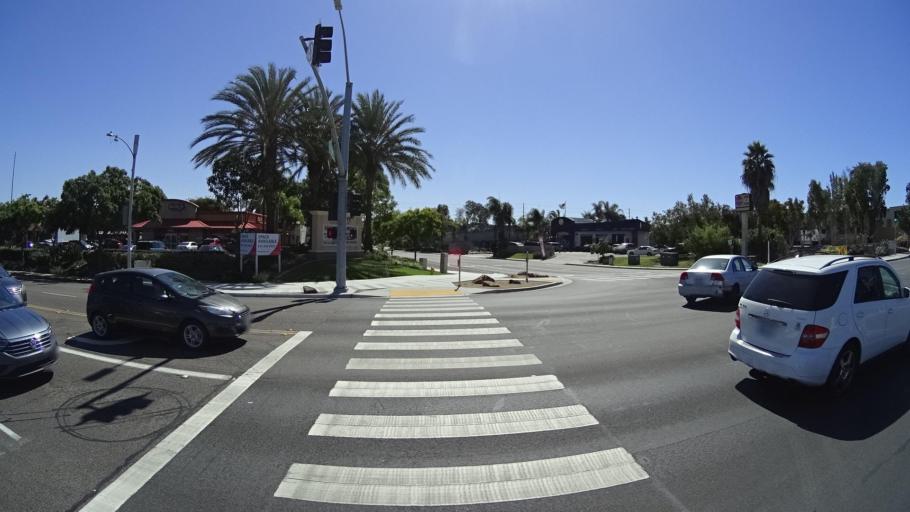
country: US
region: California
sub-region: San Diego County
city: Chula Vista
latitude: 32.6612
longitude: -117.0842
